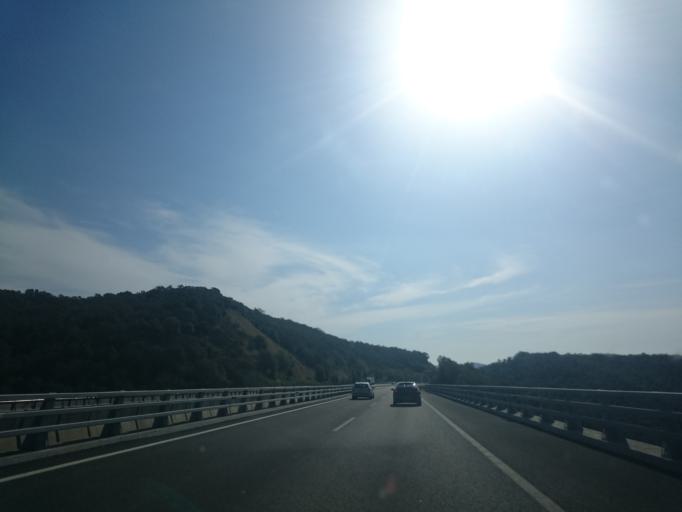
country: ES
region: Catalonia
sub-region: Provincia de Girona
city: Sant Hilari Sacalm
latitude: 41.8530
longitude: 2.4883
